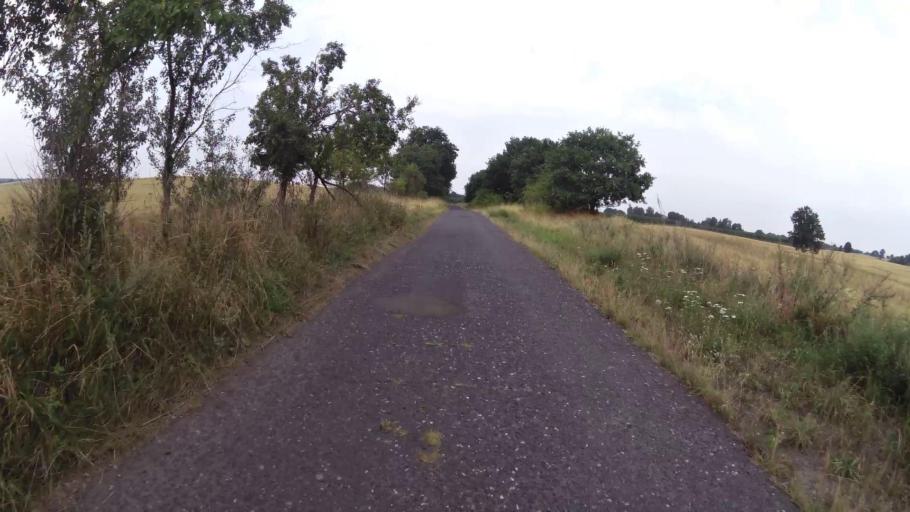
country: PL
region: West Pomeranian Voivodeship
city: Trzcinsko Zdroj
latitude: 52.9023
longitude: 14.6744
